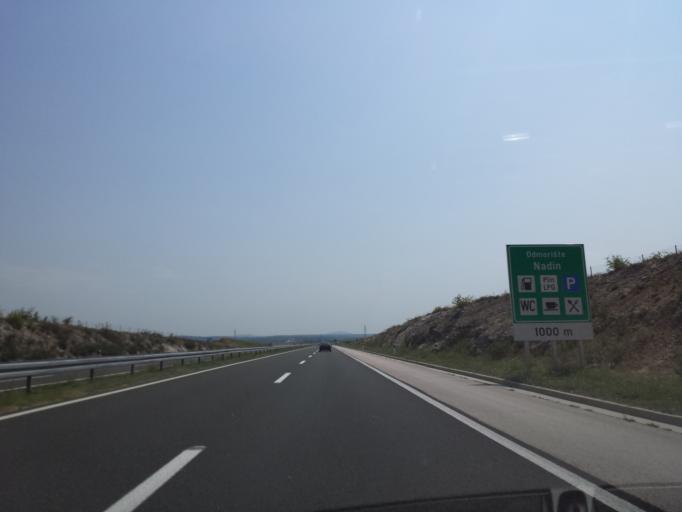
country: HR
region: Zadarska
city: Polaca
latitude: 44.0717
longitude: 15.5186
